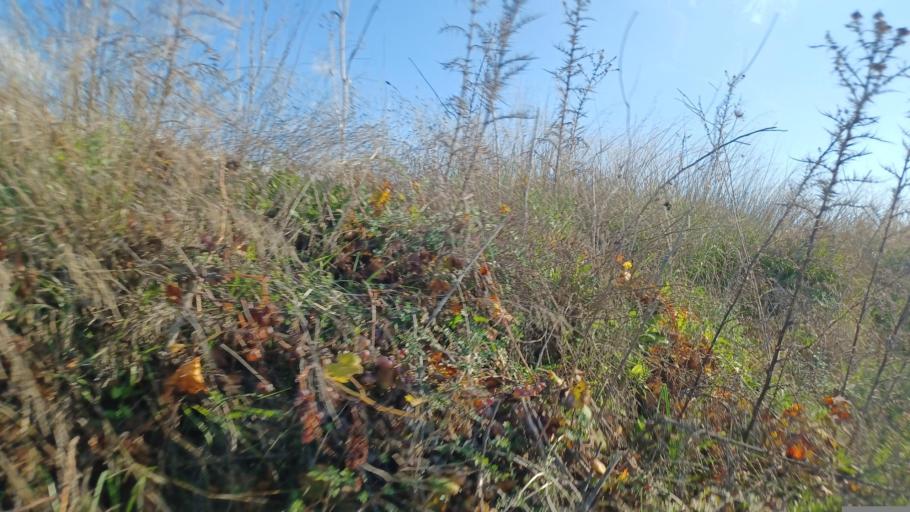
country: CY
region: Pafos
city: Mesogi
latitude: 34.8353
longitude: 32.5246
